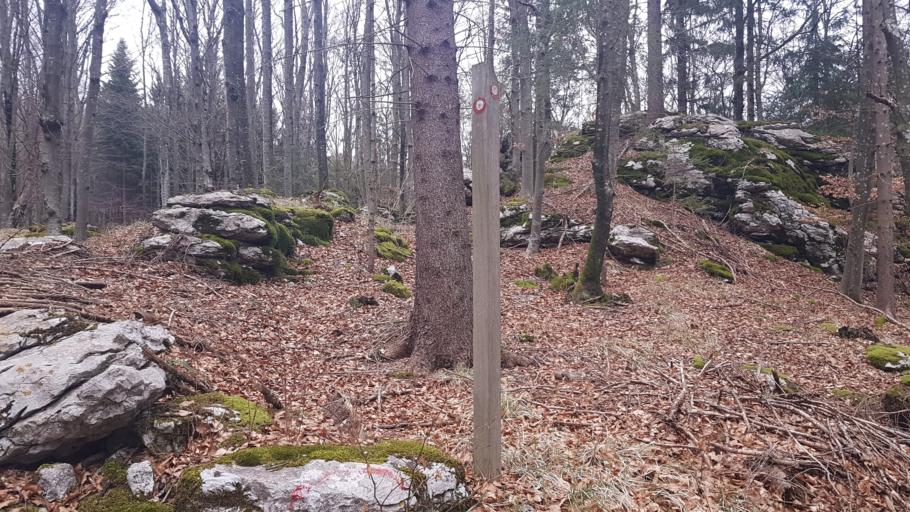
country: SI
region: Nova Gorica
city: Kromberk
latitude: 46.0375
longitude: 13.7307
